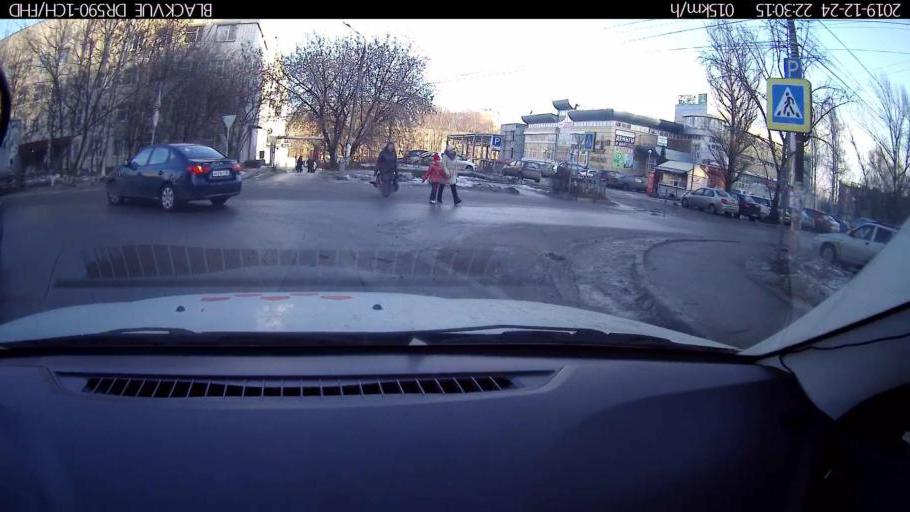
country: RU
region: Nizjnij Novgorod
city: Nizhniy Novgorod
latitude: 56.2368
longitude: 43.9611
